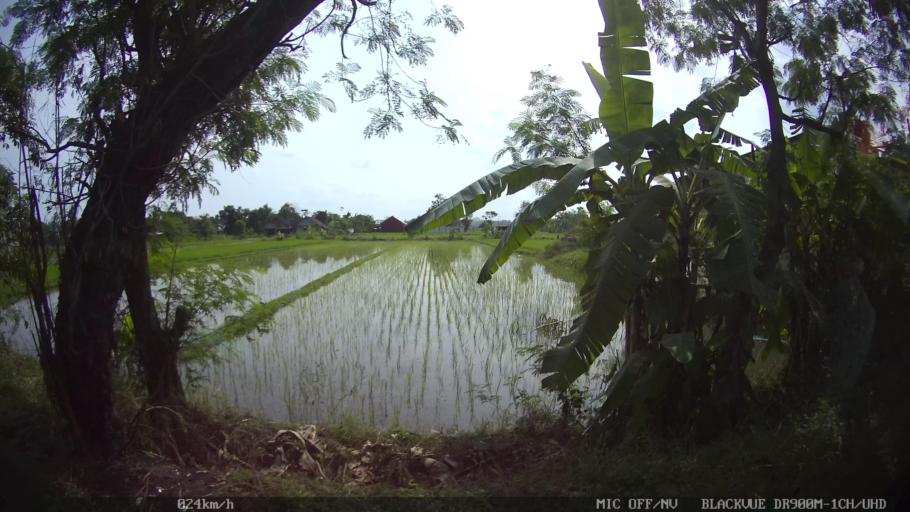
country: ID
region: Daerah Istimewa Yogyakarta
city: Depok
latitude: -7.7986
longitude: 110.4453
